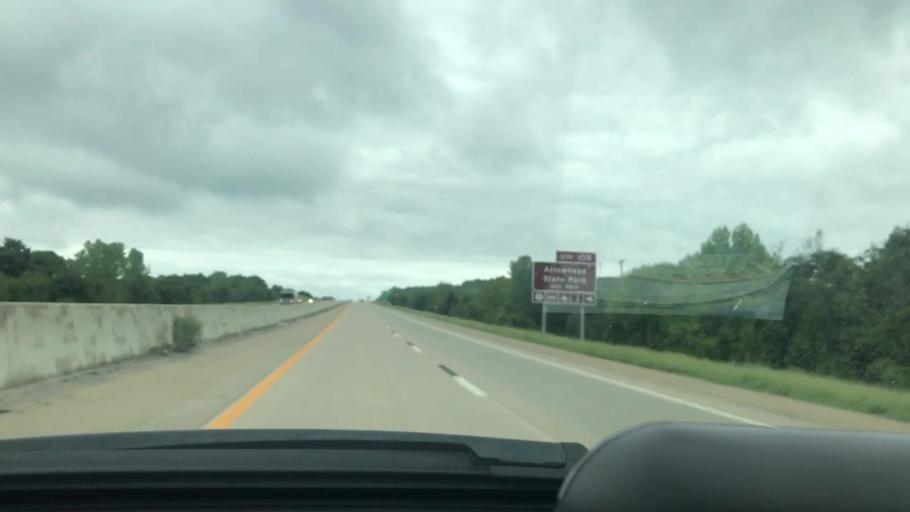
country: US
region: Oklahoma
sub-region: McIntosh County
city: Eufaula
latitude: 35.1636
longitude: -95.6539
